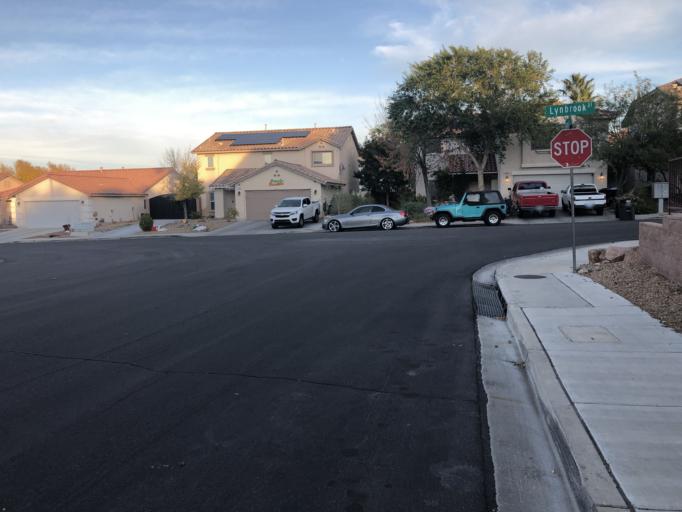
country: US
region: Nevada
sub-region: Clark County
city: Henderson
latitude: 36.0179
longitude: -115.0439
